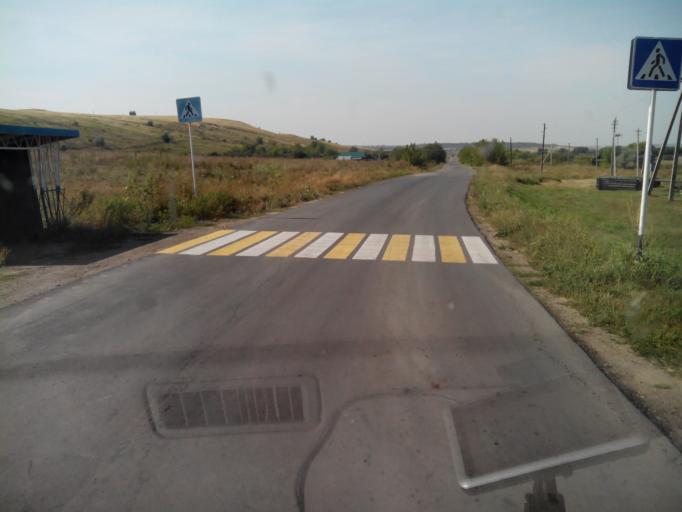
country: RU
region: Samara
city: Balasheyka
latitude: 53.1457
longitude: 48.0836
